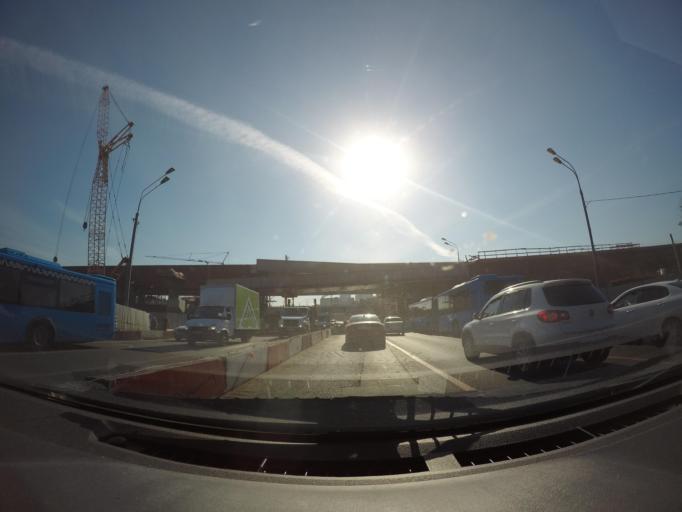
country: RU
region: Moscow
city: Tekstil'shchiki
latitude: 55.7309
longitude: 37.7235
